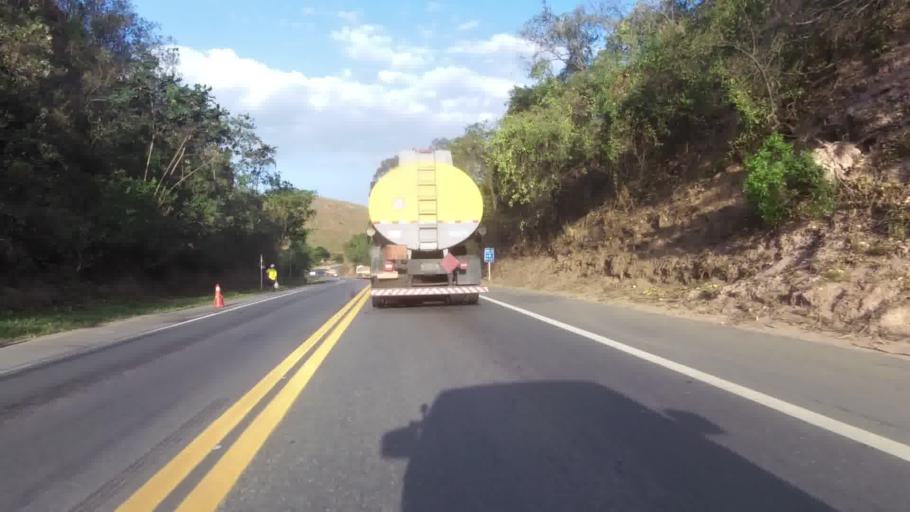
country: BR
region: Espirito Santo
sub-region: Cachoeiro De Itapemirim
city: Cachoeiro de Itapemirim
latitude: -20.8927
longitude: -41.0309
